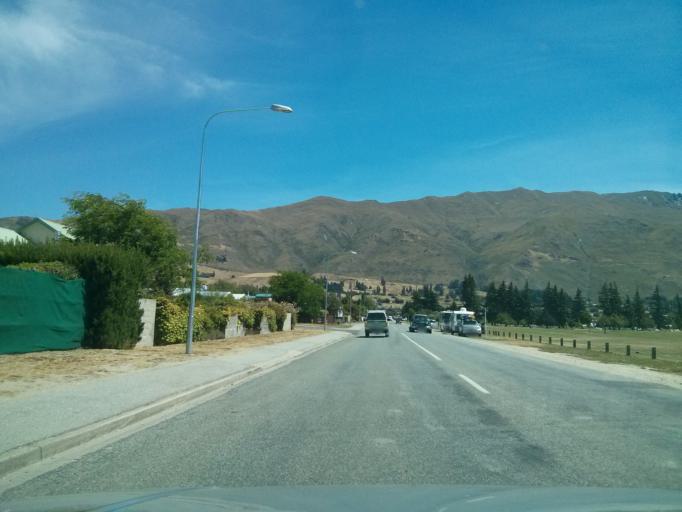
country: NZ
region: Otago
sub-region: Queenstown-Lakes District
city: Wanaka
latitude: -44.6982
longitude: 169.1336
